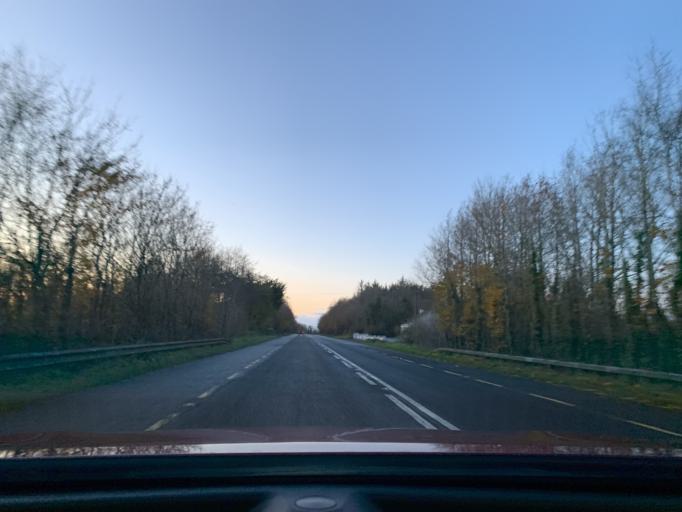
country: IE
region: Connaught
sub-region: County Leitrim
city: Carrick-on-Shannon
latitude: 53.9349
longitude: -8.0493
